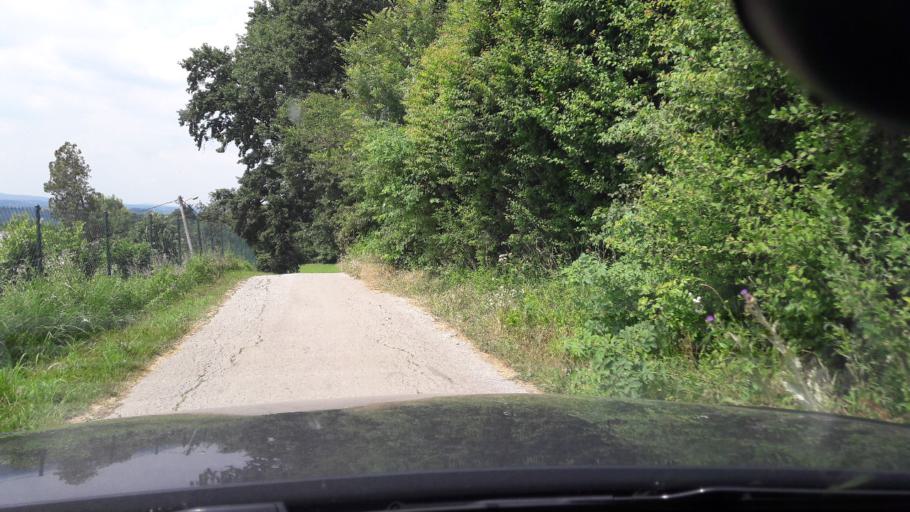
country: RS
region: Central Serbia
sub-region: Belgrade
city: Sopot
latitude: 44.6157
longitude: 20.5894
